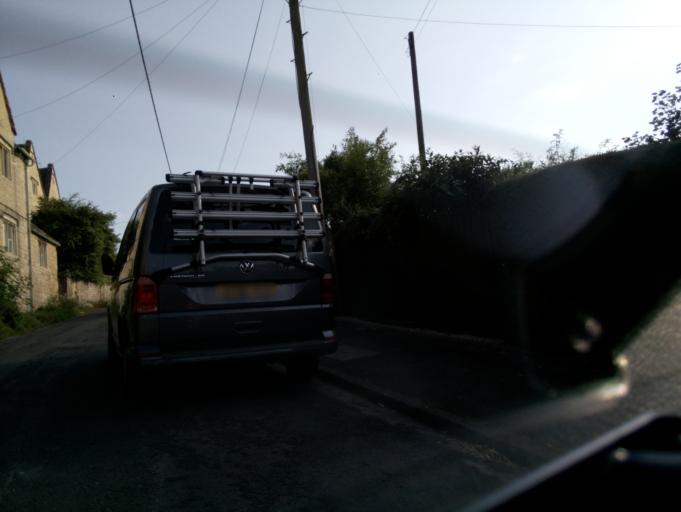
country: GB
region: England
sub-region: Gloucestershire
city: Stroud
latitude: 51.7351
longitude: -2.2268
